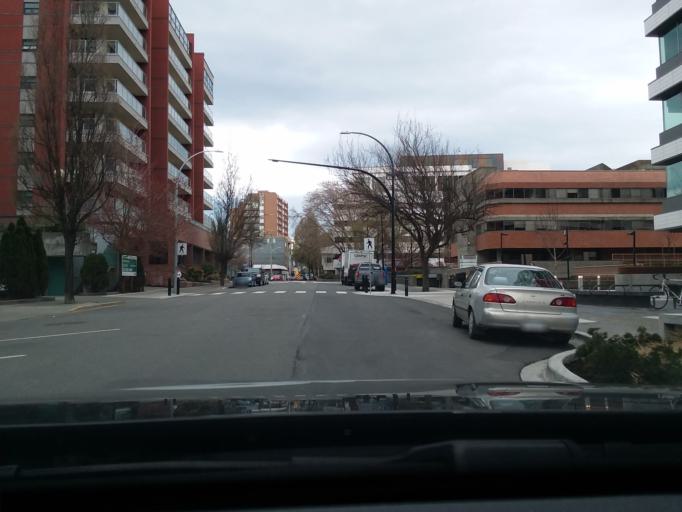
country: CA
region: British Columbia
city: Victoria
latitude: 48.4286
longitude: -123.3632
